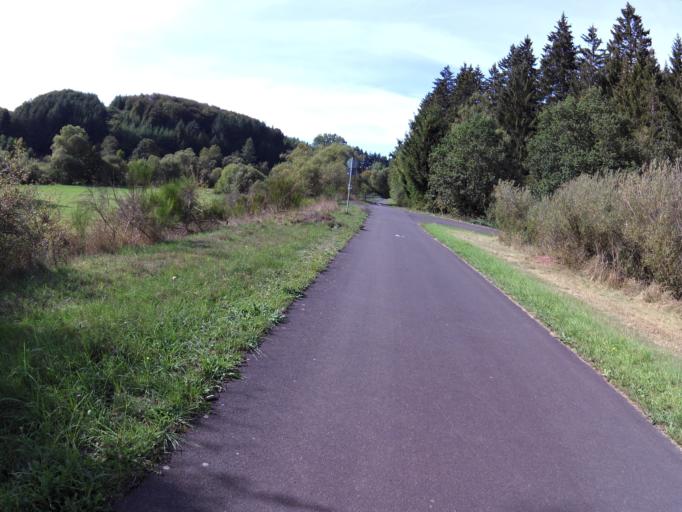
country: DE
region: Rheinland-Pfalz
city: Habscheid
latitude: 50.1930
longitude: 6.2896
